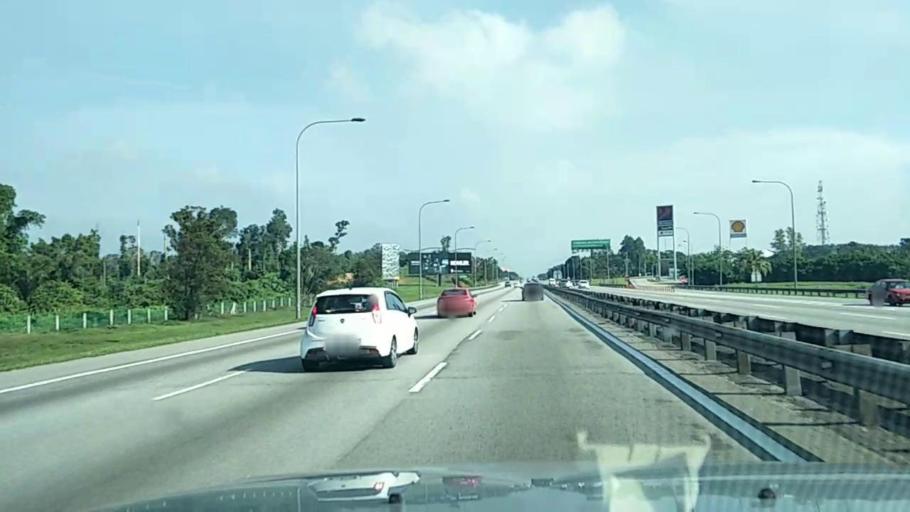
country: MY
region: Putrajaya
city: Putrajaya
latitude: 2.8988
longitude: 101.6164
